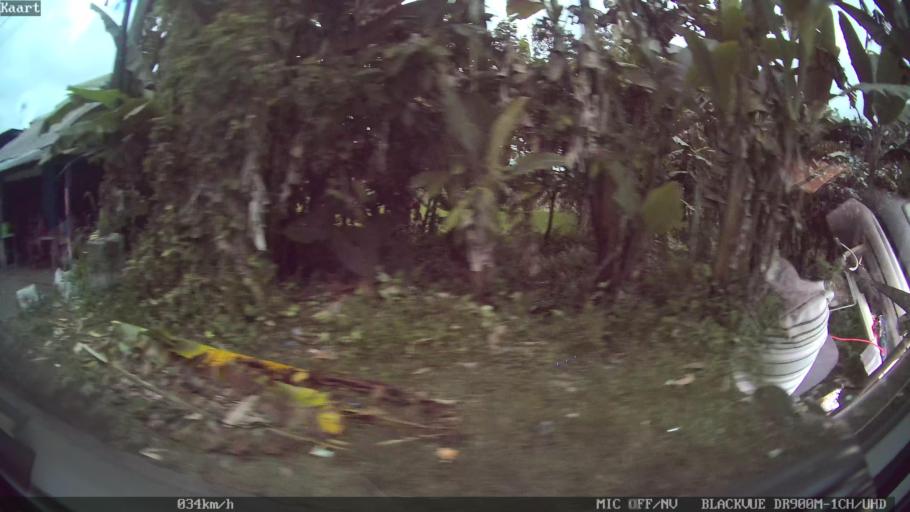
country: ID
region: Bali
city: Peneng
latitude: -8.3526
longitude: 115.2076
